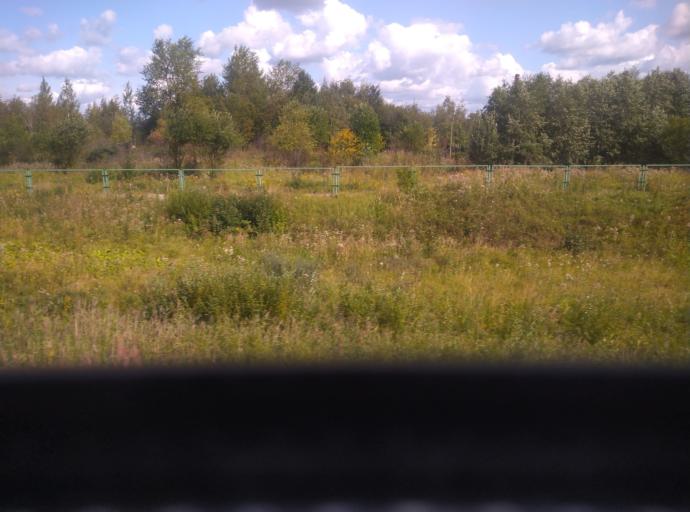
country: RU
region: St.-Petersburg
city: Kolpino
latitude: 59.7589
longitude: 30.5924
